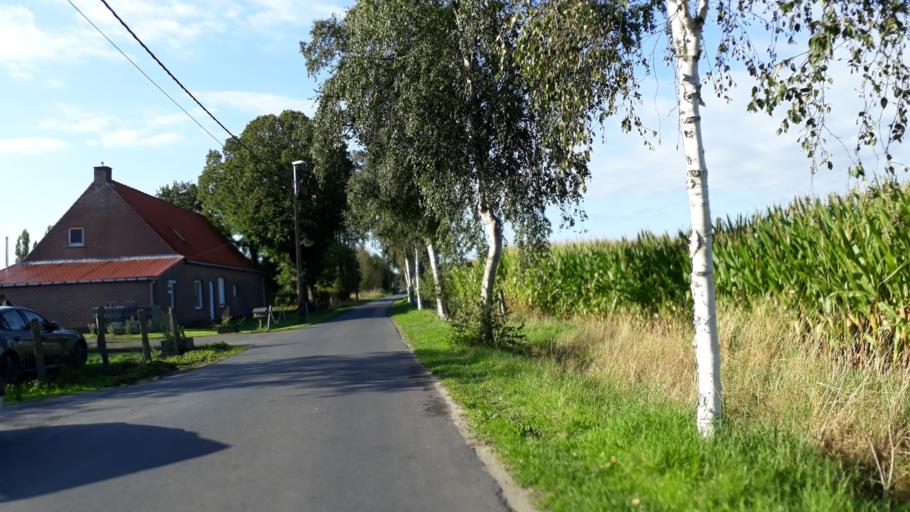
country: BE
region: Flanders
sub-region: Provincie West-Vlaanderen
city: Torhout
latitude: 51.0843
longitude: 3.1425
